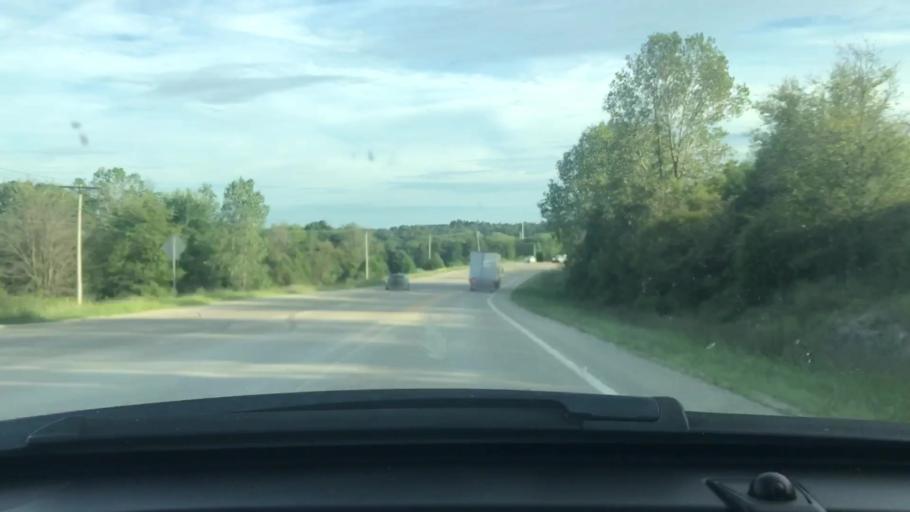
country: US
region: Arkansas
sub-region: Lawrence County
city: Hoxie
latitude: 36.1442
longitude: -91.1586
